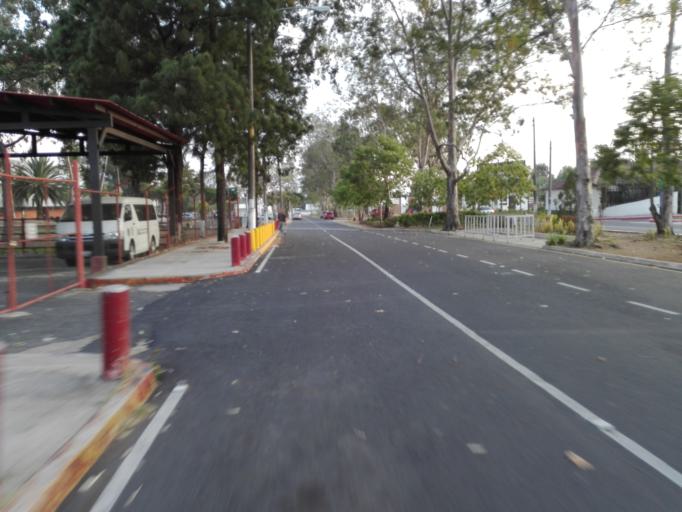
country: GT
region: Guatemala
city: Santa Catarina Pinula
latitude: 14.5838
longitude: -90.5566
